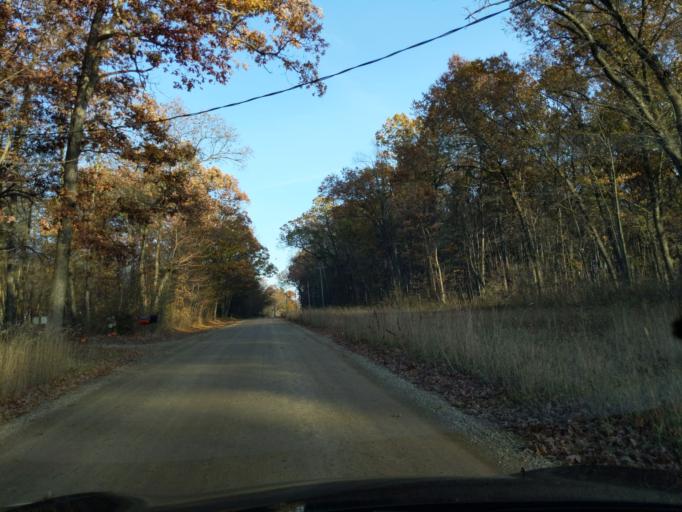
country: US
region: Michigan
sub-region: Clinton County
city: Bath
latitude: 42.7986
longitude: -84.4878
